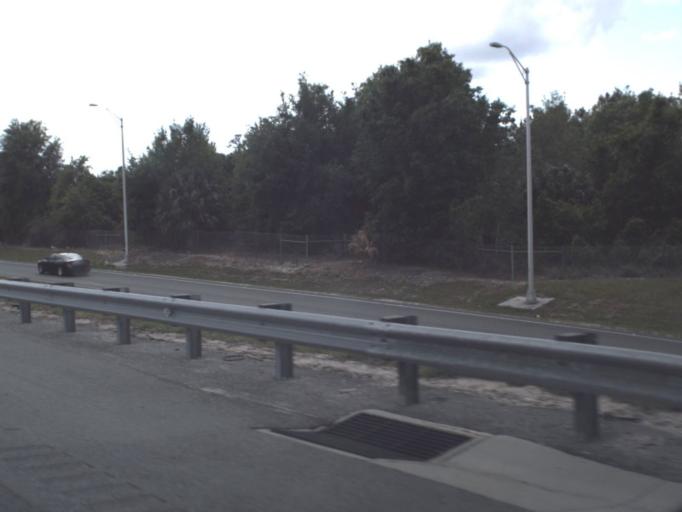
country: US
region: Florida
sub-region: Orange County
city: Paradise Heights
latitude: 28.6323
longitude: -81.5410
